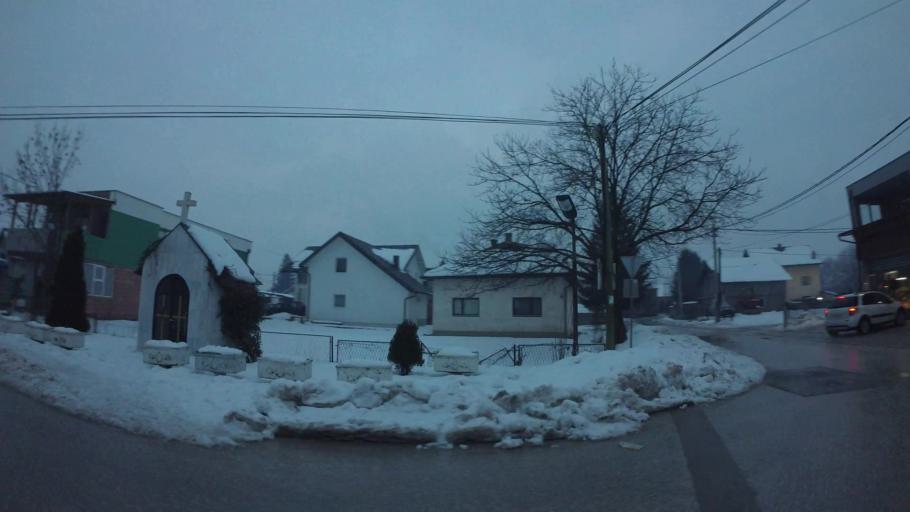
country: BA
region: Federation of Bosnia and Herzegovina
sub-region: Kanton Sarajevo
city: Sarajevo
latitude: 43.8531
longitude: 18.2952
